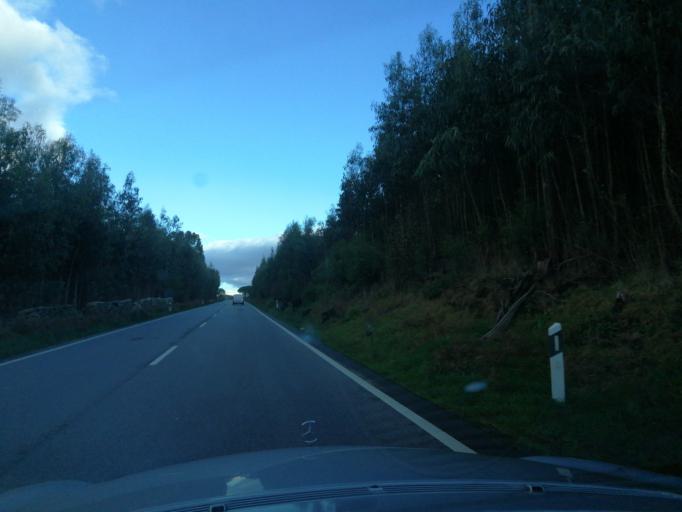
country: PT
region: Braga
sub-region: Barcelos
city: Vila Frescainha
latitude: 41.5728
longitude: -8.7044
